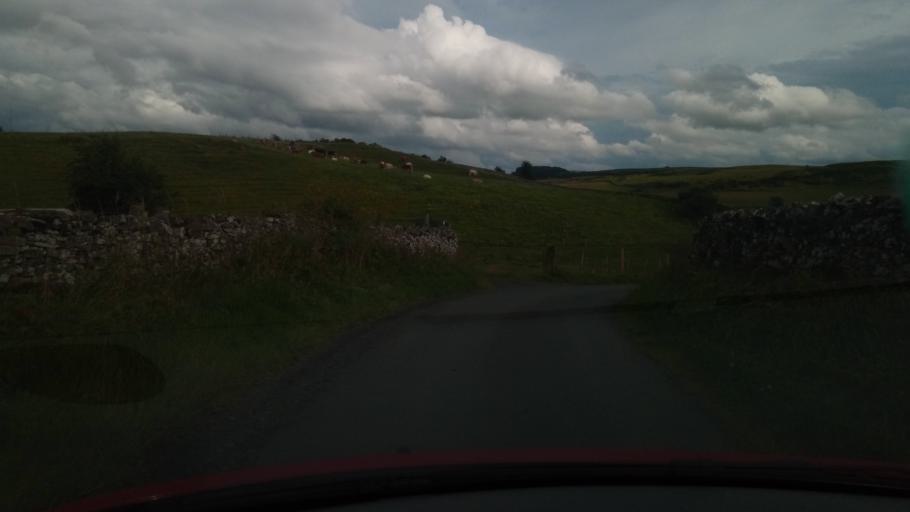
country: GB
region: Scotland
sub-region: The Scottish Borders
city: Hawick
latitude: 55.4167
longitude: -2.7774
